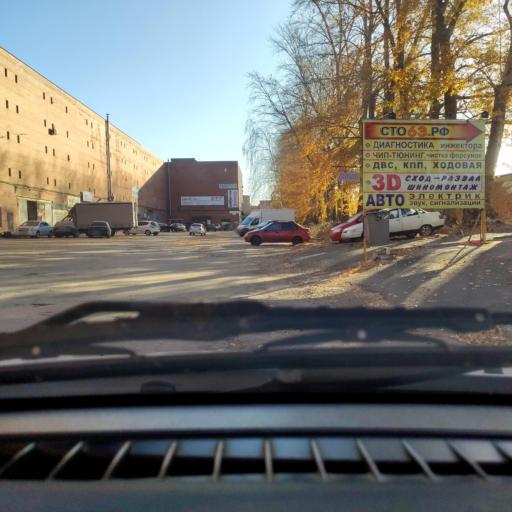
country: RU
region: Samara
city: Tol'yatti
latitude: 53.5395
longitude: 49.3027
